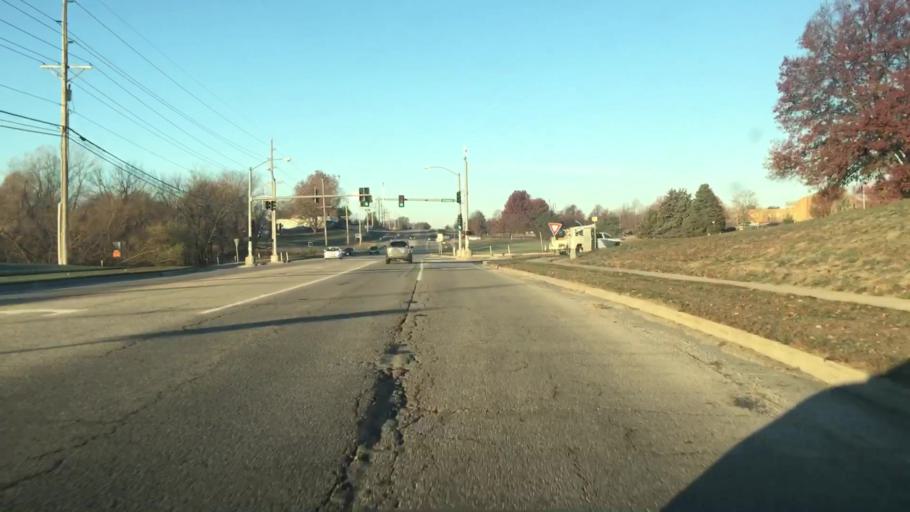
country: US
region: Missouri
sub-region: Buchanan County
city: Saint Joseph
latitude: 39.7555
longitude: -94.7818
